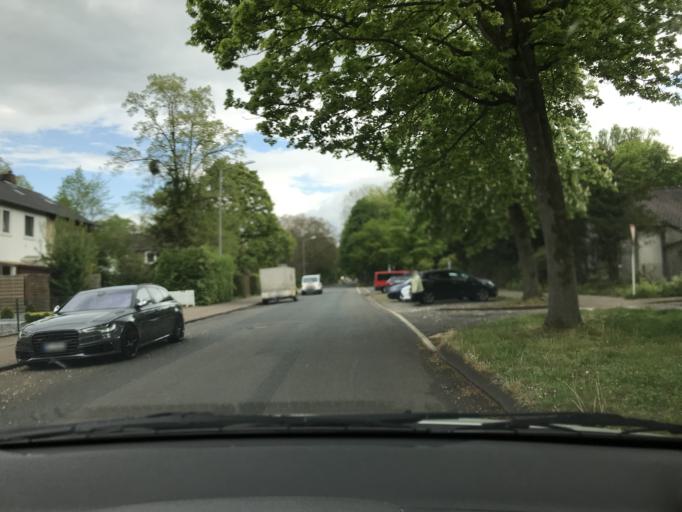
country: DE
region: North Rhine-Westphalia
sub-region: Regierungsbezirk Detmold
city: Minden
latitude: 52.2806
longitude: 8.8941
